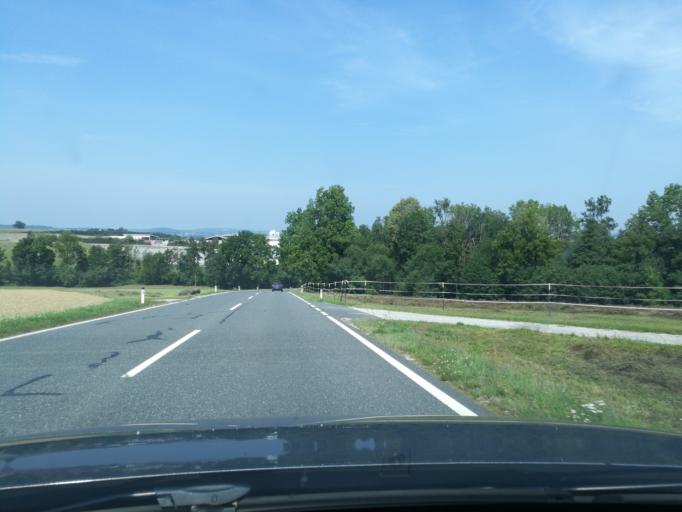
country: AT
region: Upper Austria
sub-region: Politischer Bezirk Grieskirchen
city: Grieskirchen
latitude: 48.3176
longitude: 13.7764
